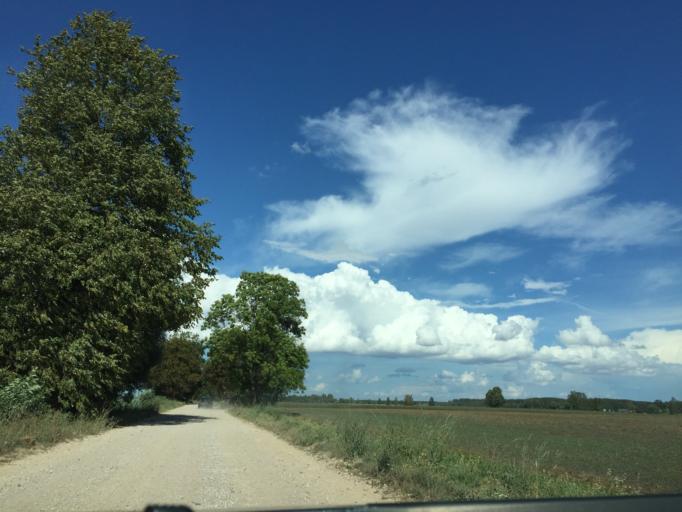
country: LT
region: Siauliu apskritis
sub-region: Joniskis
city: Joniskis
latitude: 56.3472
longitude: 23.5510
